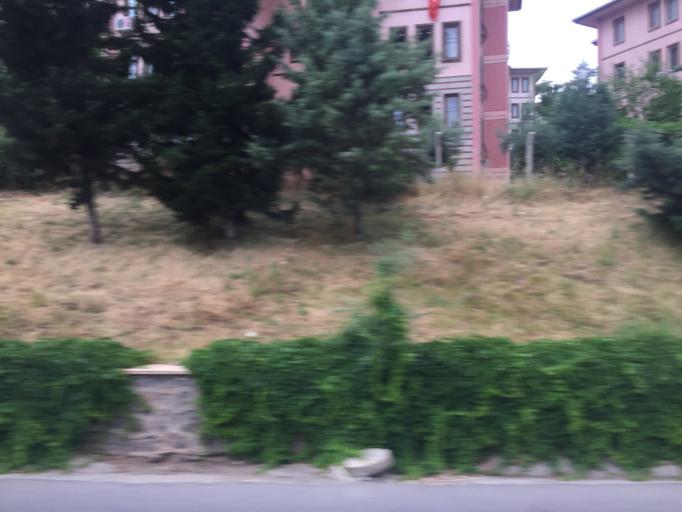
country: TR
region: Gaziantep
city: Gaziantep
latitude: 37.0437
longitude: 37.4248
